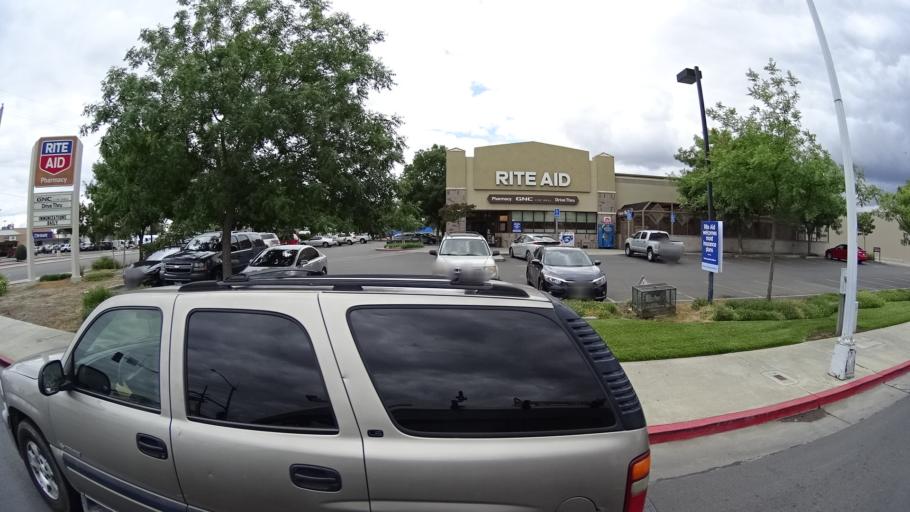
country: US
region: California
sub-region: Kings County
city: Hanford
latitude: 36.3279
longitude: -119.6557
